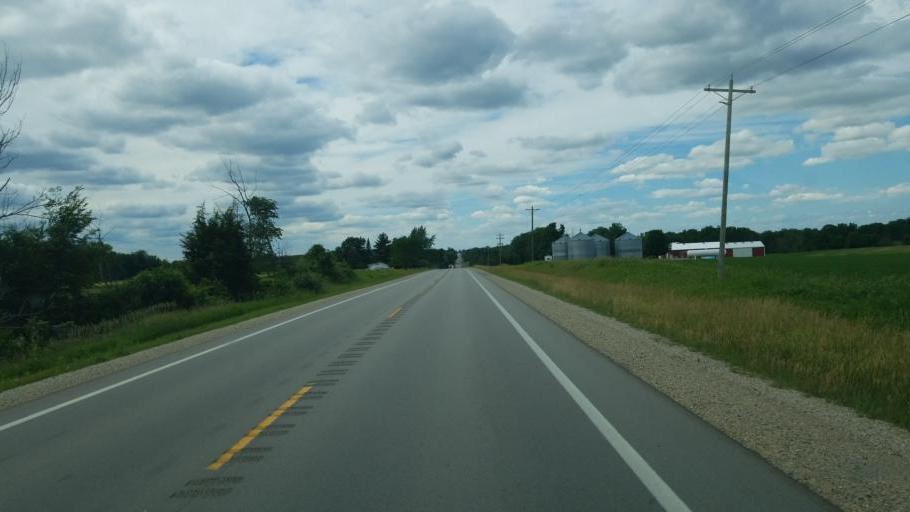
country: US
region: Michigan
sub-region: Eaton County
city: Charlotte
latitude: 42.6317
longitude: -84.8725
